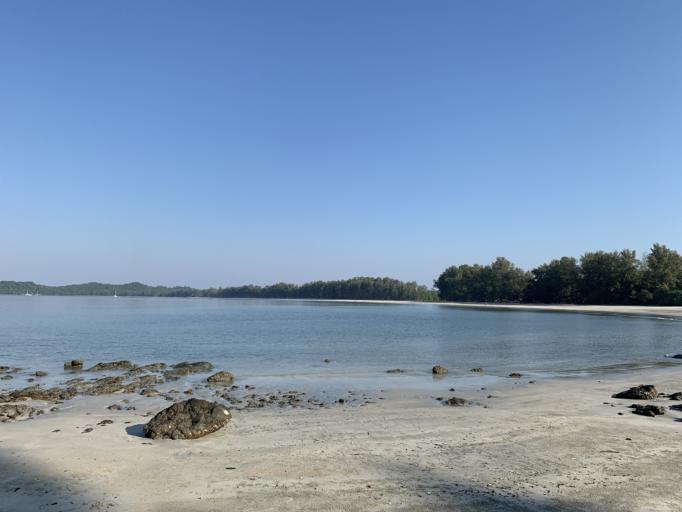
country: TH
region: Ranong
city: Kapoe
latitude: 9.7107
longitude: 98.3961
